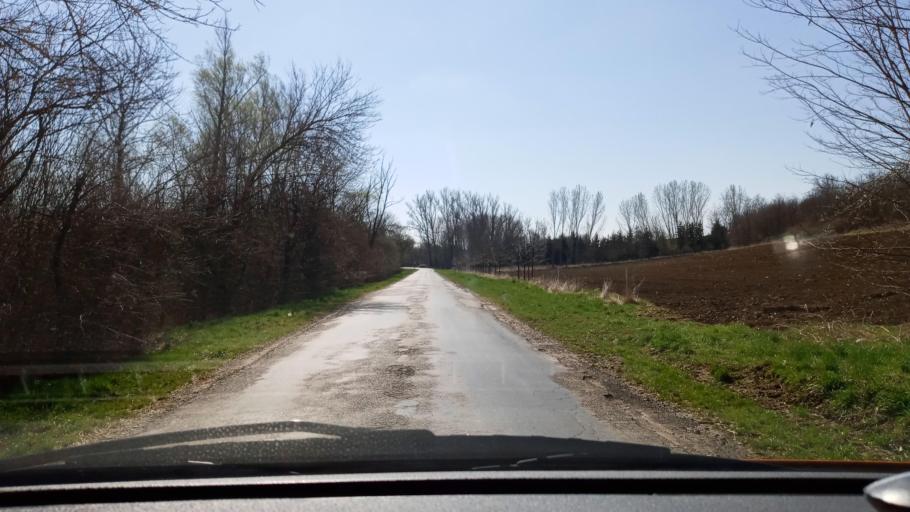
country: HU
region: Baranya
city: Kozarmisleny
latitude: 46.0691
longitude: 18.3665
